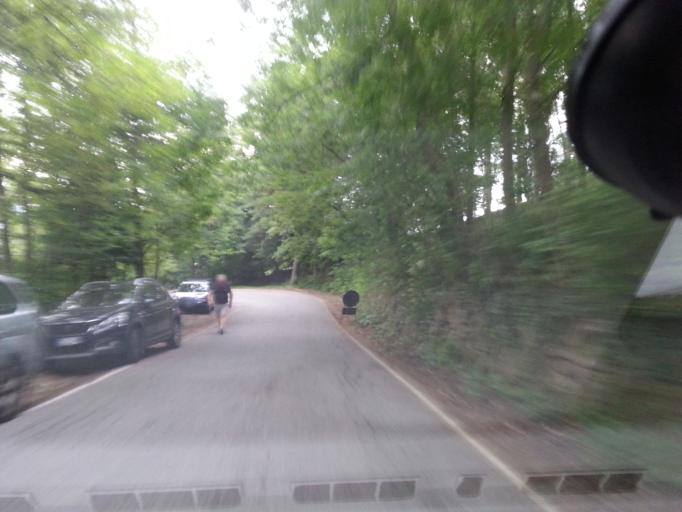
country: IT
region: Piedmont
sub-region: Provincia di Torino
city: Chiusa di San Michele
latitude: 45.0929
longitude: 7.3401
